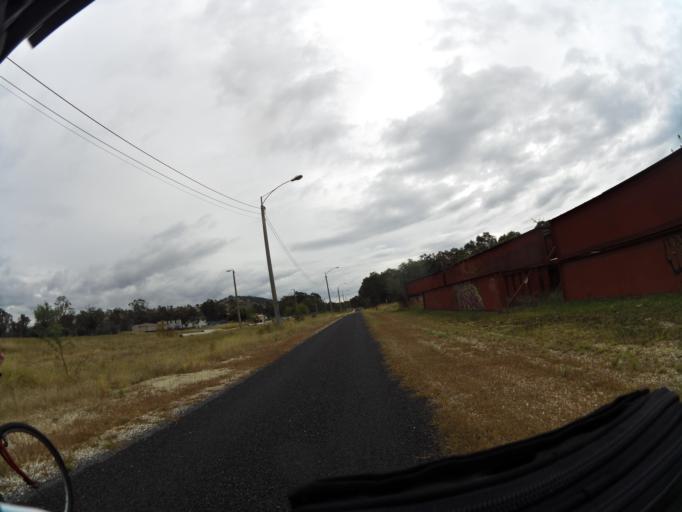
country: AU
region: Victoria
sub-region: Wodonga
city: Wodonga
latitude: -36.1494
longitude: 146.9381
